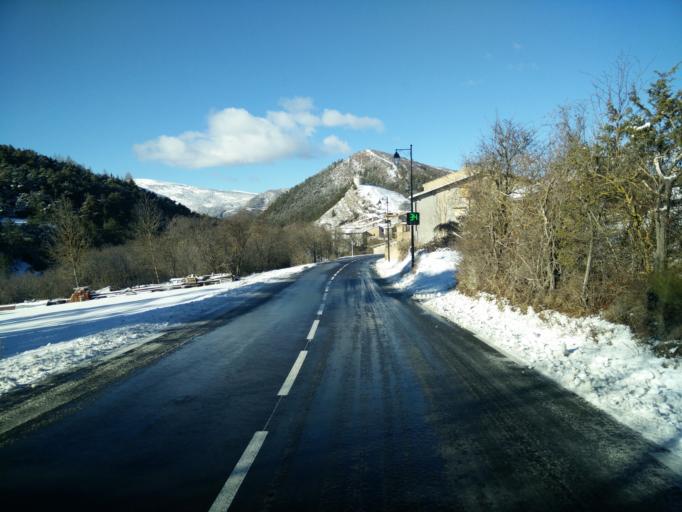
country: FR
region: Provence-Alpes-Cote d'Azur
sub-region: Departement des Alpes-de-Haute-Provence
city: Annot
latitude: 43.9130
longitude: 6.5903
